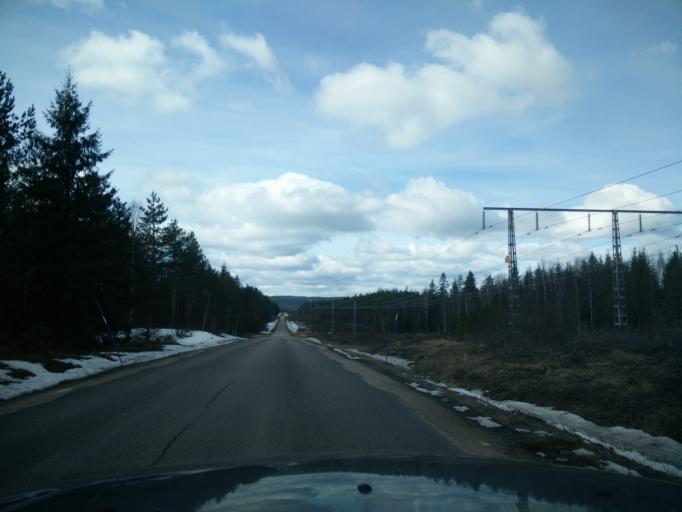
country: SE
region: Vaermland
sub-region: Hagfors Kommun
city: Hagfors
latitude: 60.0350
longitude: 13.5596
